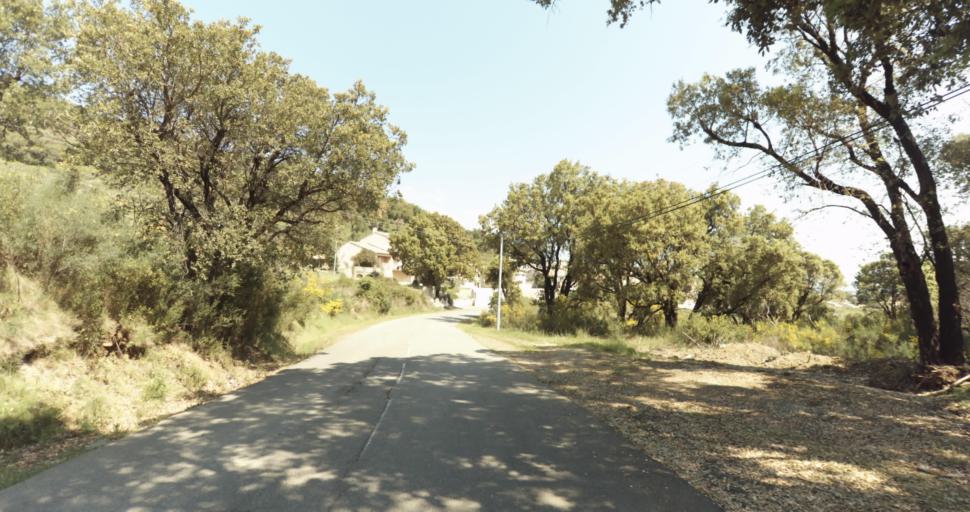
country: FR
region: Corsica
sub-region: Departement de la Haute-Corse
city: Biguglia
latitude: 42.6168
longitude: 9.4234
